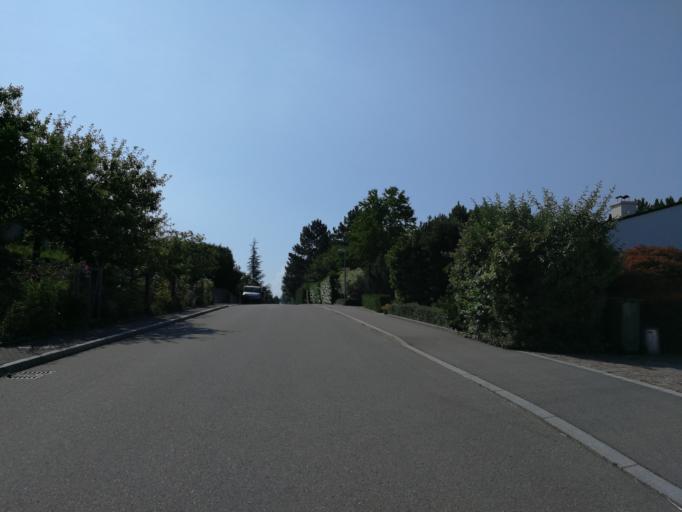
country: CH
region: Zurich
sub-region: Bezirk Meilen
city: Herrliberg
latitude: 47.2974
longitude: 8.6127
